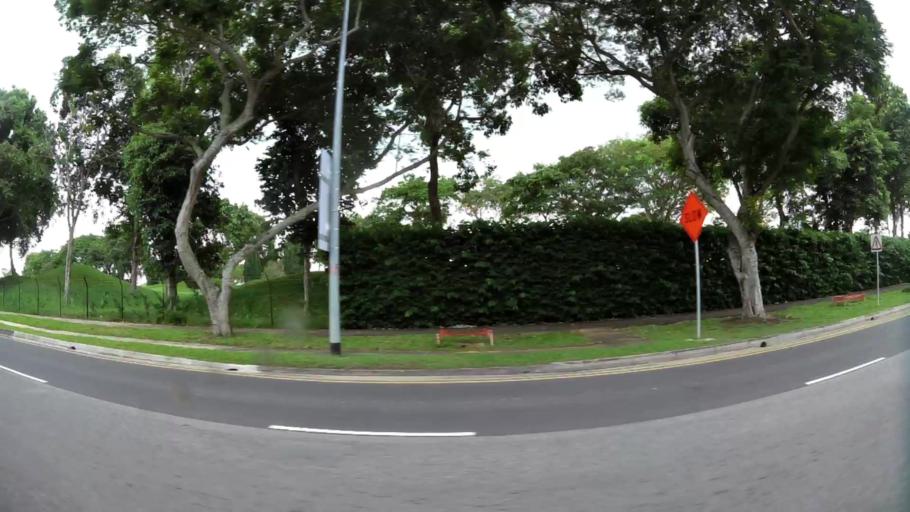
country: SG
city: Singapore
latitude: 1.3285
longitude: 103.9657
